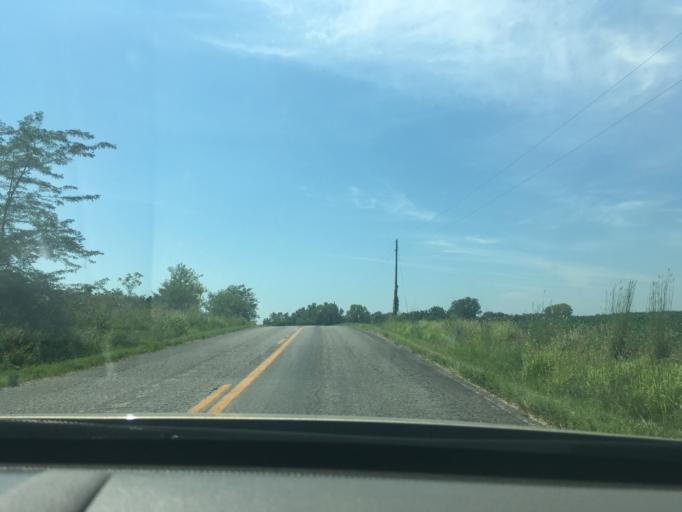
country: US
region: Missouri
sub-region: Gentry County
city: Stanberry
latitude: 40.2182
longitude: -94.7273
